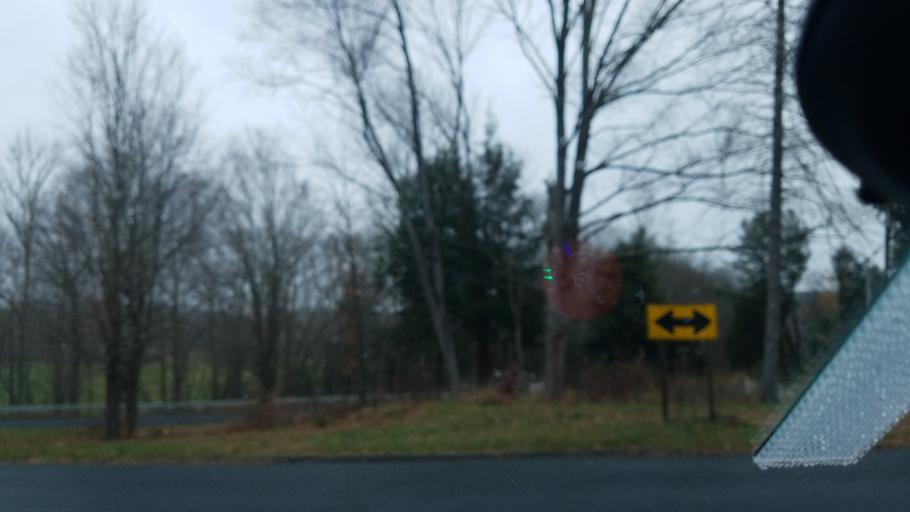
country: US
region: Connecticut
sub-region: Litchfield County
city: Woodbury Center
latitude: 41.5520
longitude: -73.1975
